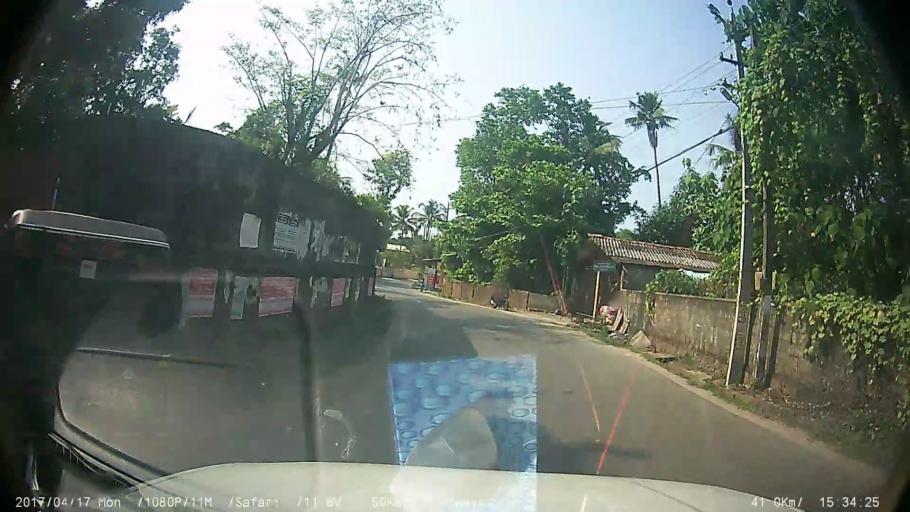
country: IN
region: Kerala
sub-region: Ernakulam
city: Ramamangalam
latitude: 9.9732
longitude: 76.4272
